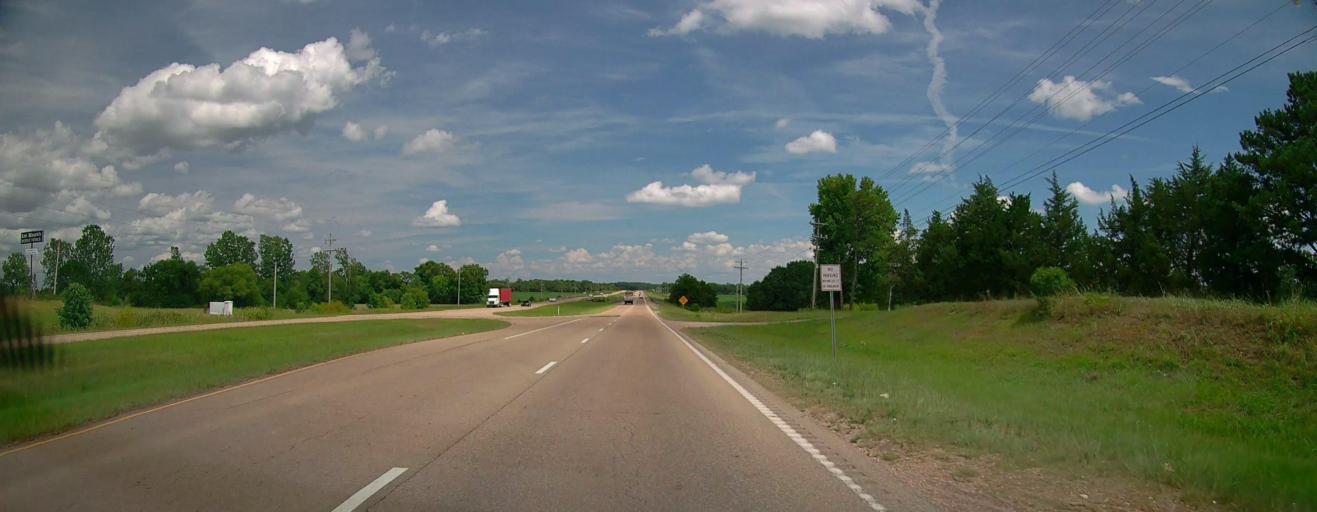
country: US
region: Mississippi
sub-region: Lee County
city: Shannon
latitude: 34.1044
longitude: -88.6682
